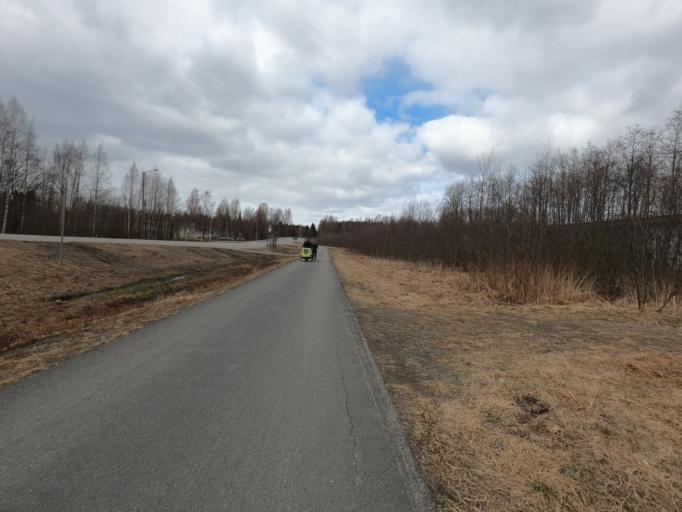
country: FI
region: North Karelia
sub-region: Joensuu
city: Joensuu
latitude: 62.5735
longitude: 29.8031
